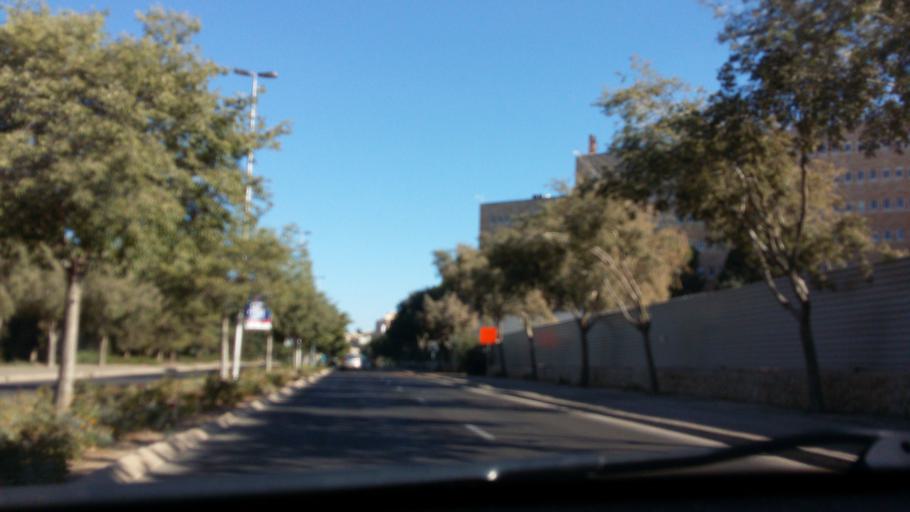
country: IL
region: Jerusalem
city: Jerusalem
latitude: 31.7767
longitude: 35.2027
